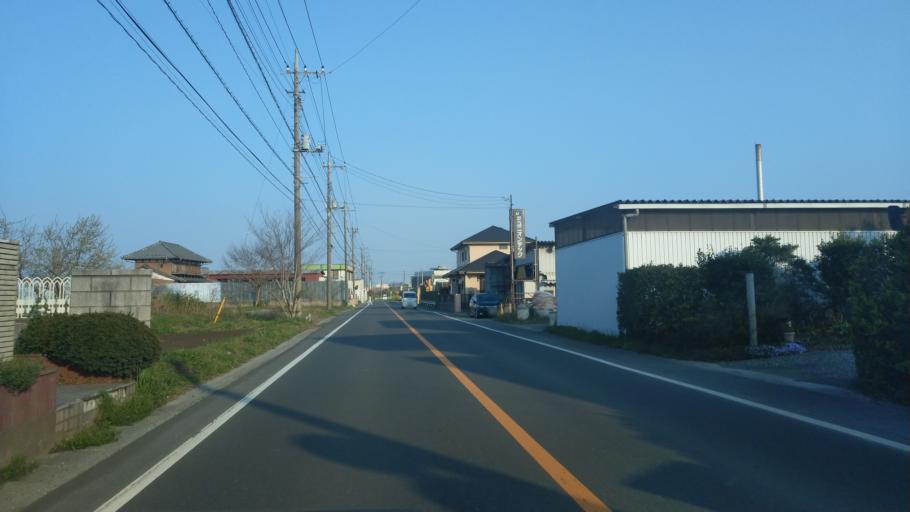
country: JP
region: Saitama
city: Okegawa
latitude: 36.0293
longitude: 139.5842
